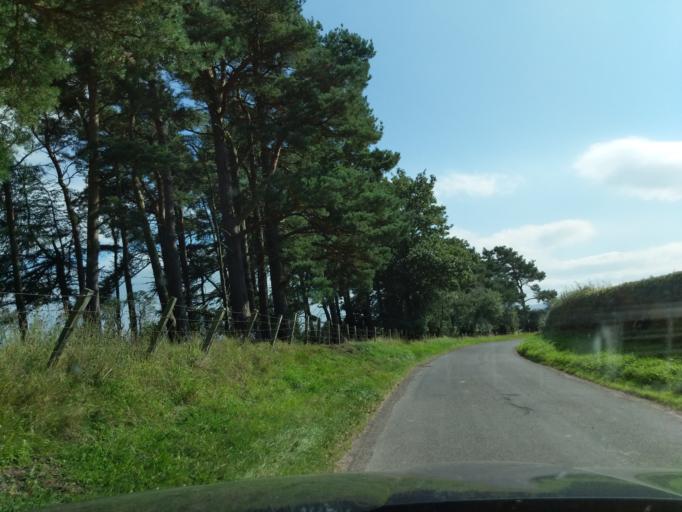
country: GB
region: England
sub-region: Northumberland
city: Ford
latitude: 55.6430
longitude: -2.1369
